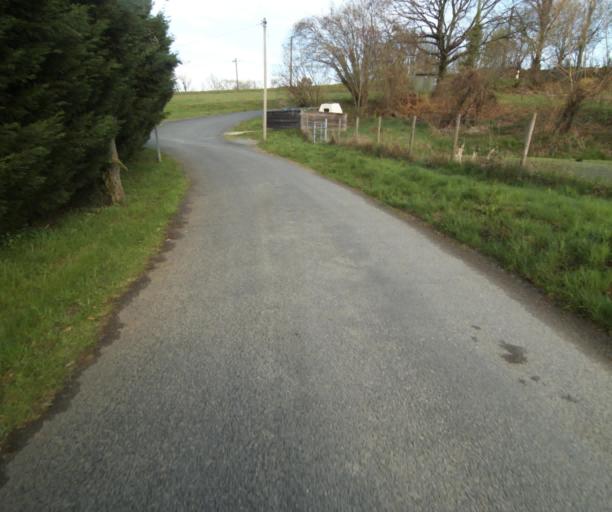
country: FR
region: Limousin
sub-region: Departement de la Correze
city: Correze
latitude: 45.3567
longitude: 1.8443
